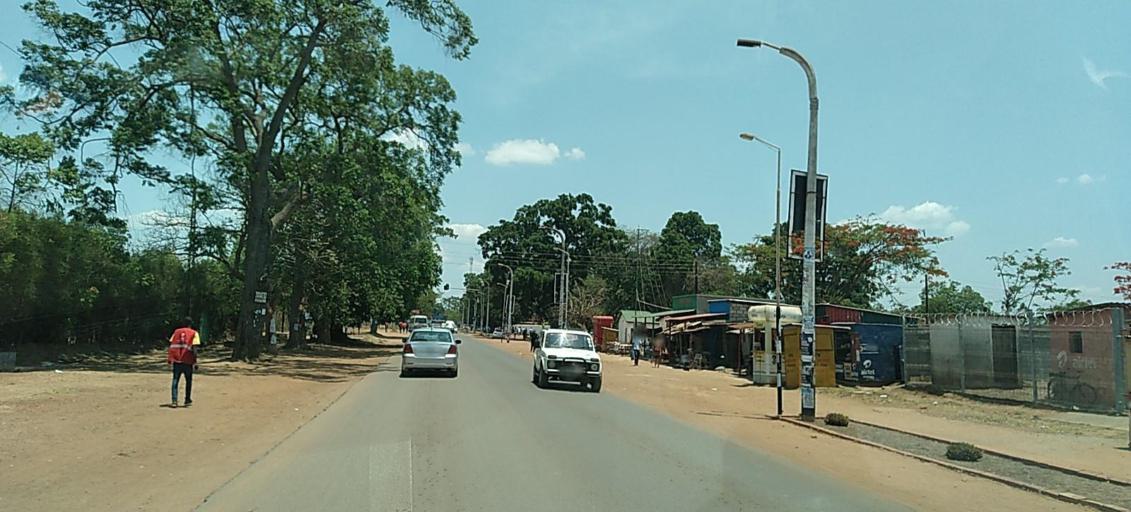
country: ZM
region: Copperbelt
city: Luanshya
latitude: -13.1349
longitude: 28.4201
